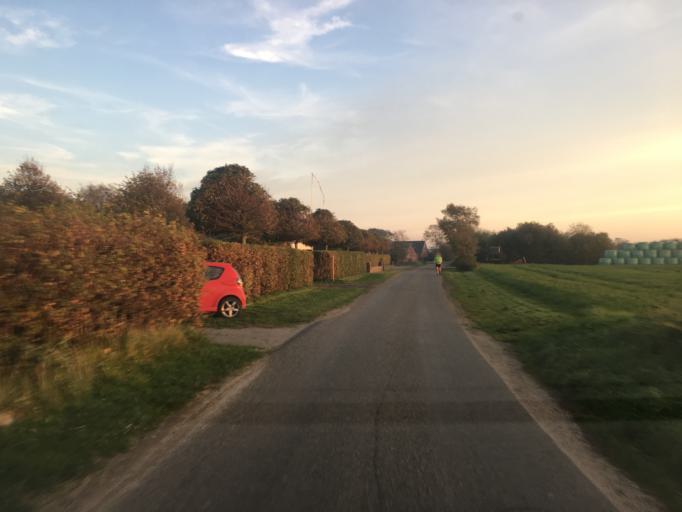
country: DK
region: South Denmark
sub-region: Tonder Kommune
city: Logumkloster
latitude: 55.0109
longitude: 9.0928
